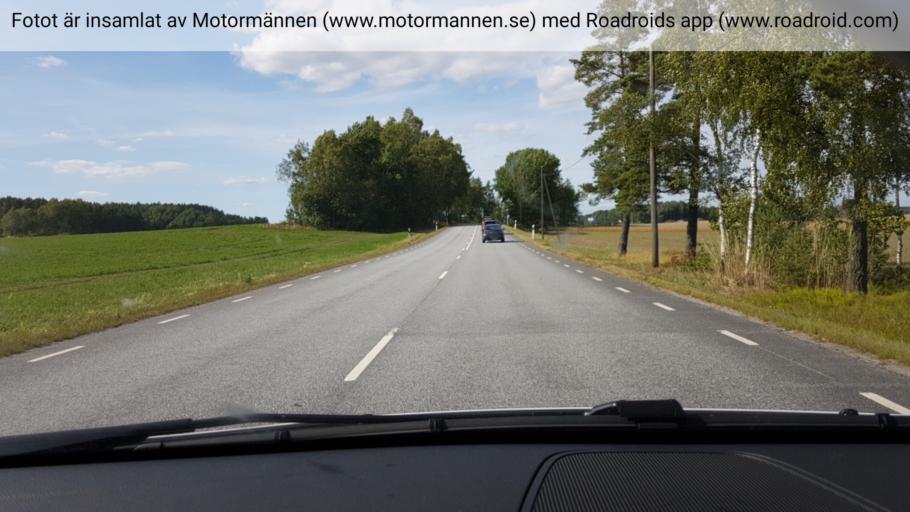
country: SE
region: Stockholm
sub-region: Sodertalje Kommun
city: Pershagen
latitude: 59.0619
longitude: 17.6100
